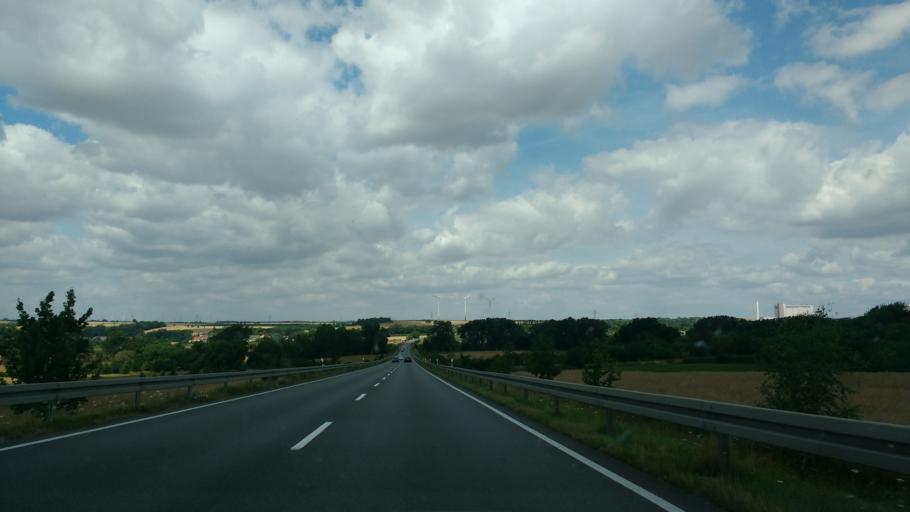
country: DE
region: Saxony-Anhalt
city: Zeitz
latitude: 51.0370
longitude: 12.1163
